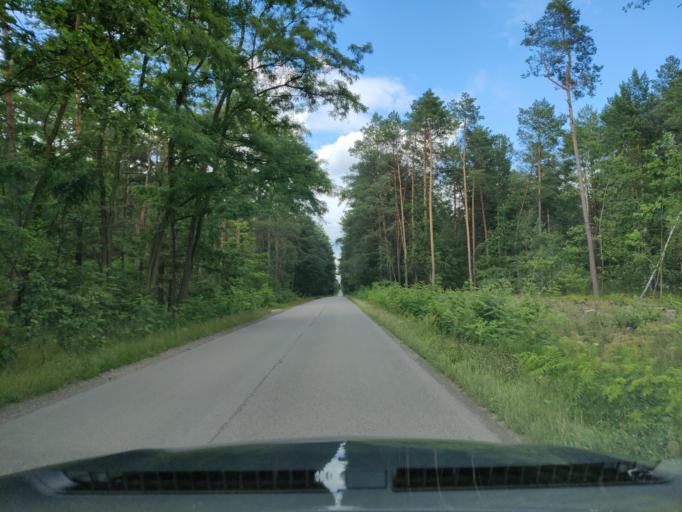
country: PL
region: Masovian Voivodeship
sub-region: Powiat wegrowski
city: Miedzna
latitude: 52.5291
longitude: 22.0782
